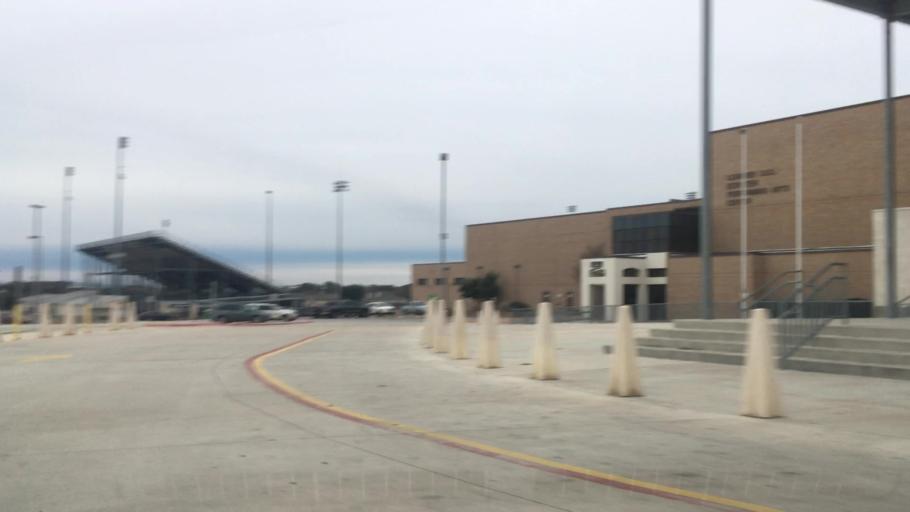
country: US
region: Texas
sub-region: Williamson County
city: Leander
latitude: 30.5388
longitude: -97.8504
